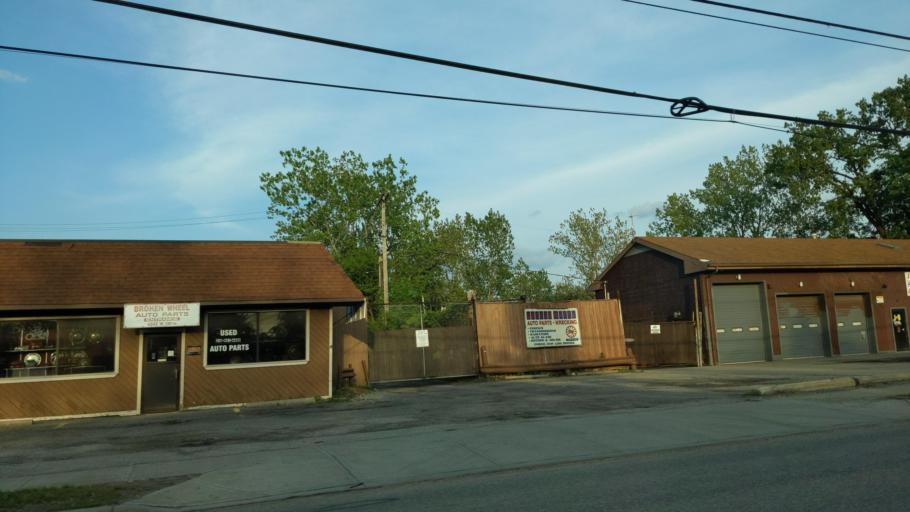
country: US
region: Ohio
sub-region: Cuyahoga County
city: Brooklyn
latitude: 41.4363
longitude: -81.7800
